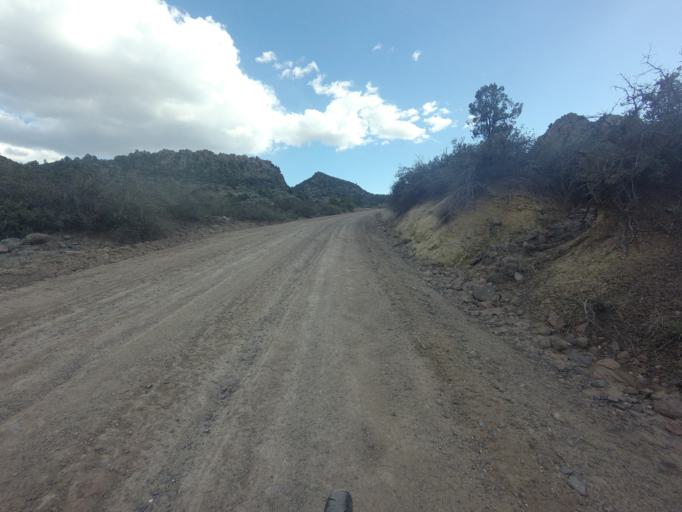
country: US
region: Arizona
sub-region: Yavapai County
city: Camp Verde
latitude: 34.4397
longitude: -111.6872
